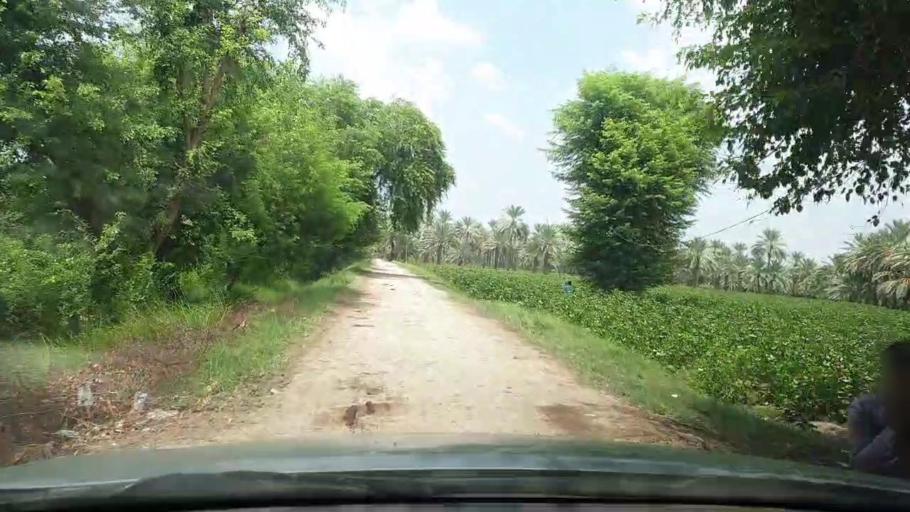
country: PK
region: Sindh
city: Kot Diji
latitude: 27.4244
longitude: 68.7679
